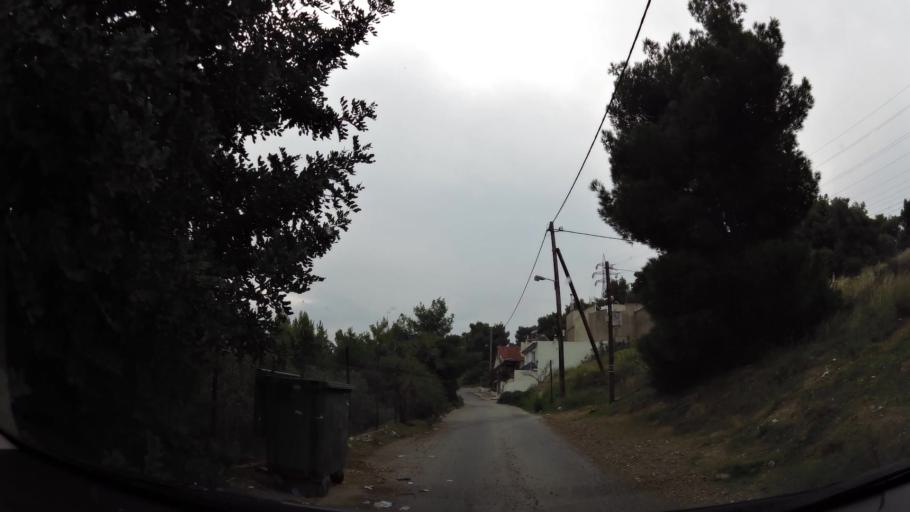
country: GR
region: Attica
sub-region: Nomos Piraios
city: Korydallos
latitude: 38.0005
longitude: 23.6467
